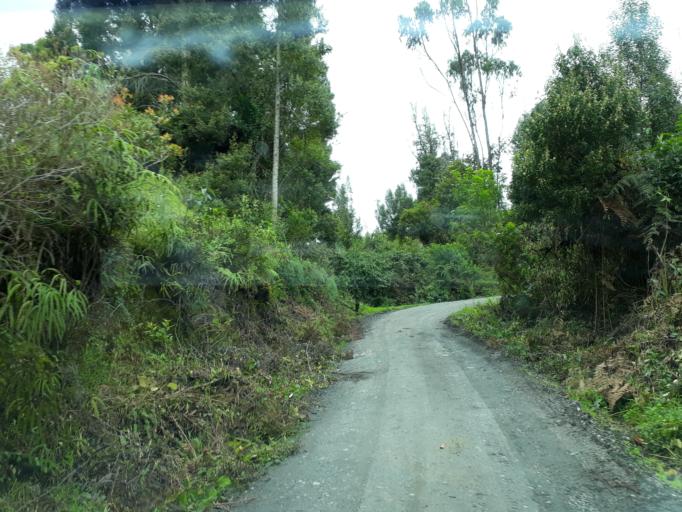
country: CO
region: Cundinamarca
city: Junin
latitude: 4.6495
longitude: -73.6627
